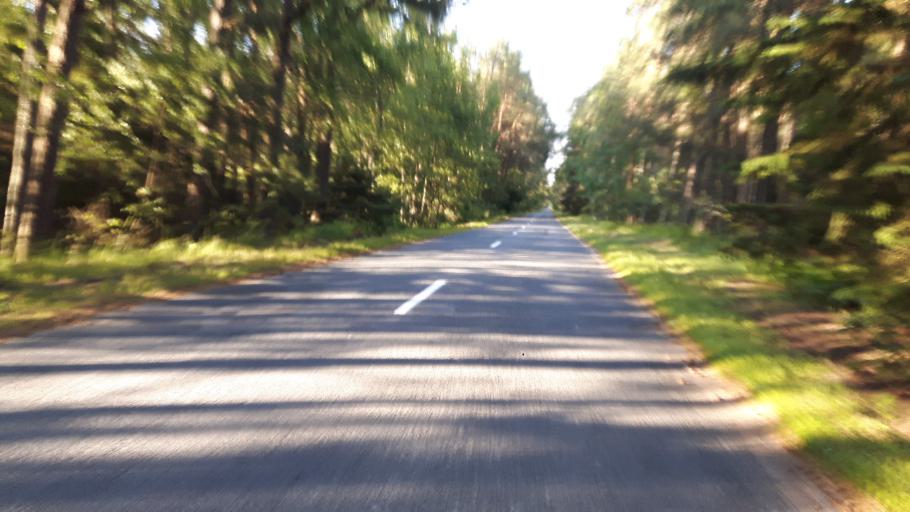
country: LT
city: Nida
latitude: 55.2525
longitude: 20.9292
